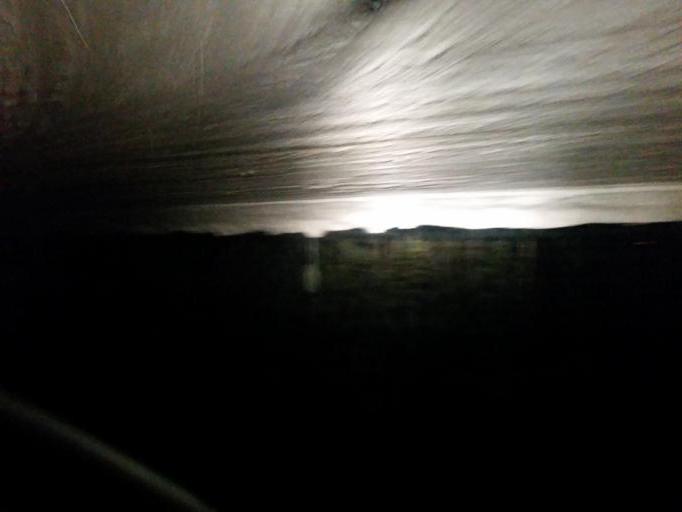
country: SE
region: Norrbotten
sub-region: Pitea Kommun
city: Roknas
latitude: 65.5044
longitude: 21.1943
